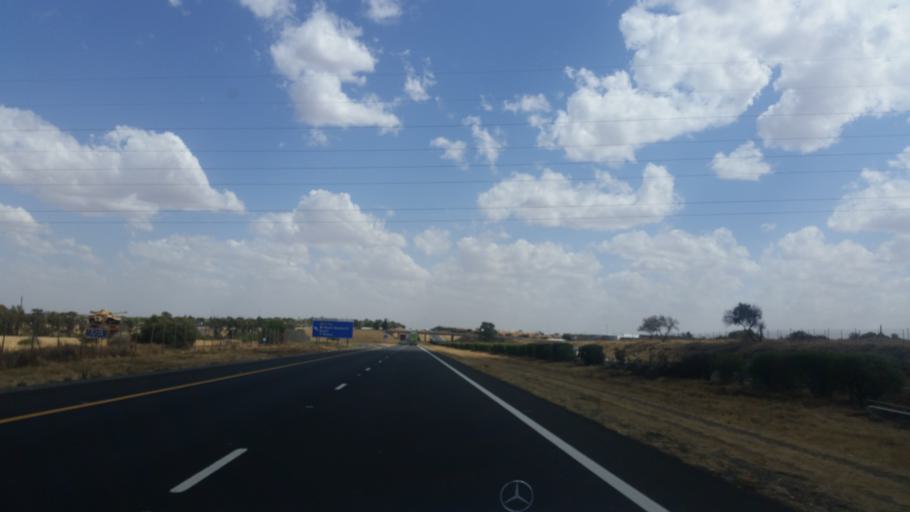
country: ZA
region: Orange Free State
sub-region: Mangaung Metropolitan Municipality
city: Bloemfontein
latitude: -29.0856
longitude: 26.1746
